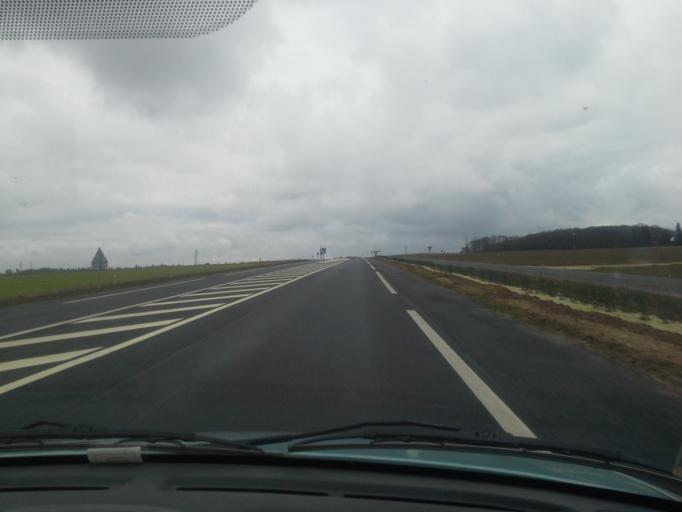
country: FR
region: Centre
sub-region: Departement du Loir-et-Cher
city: Naveil
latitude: 47.7732
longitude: 1.0439
